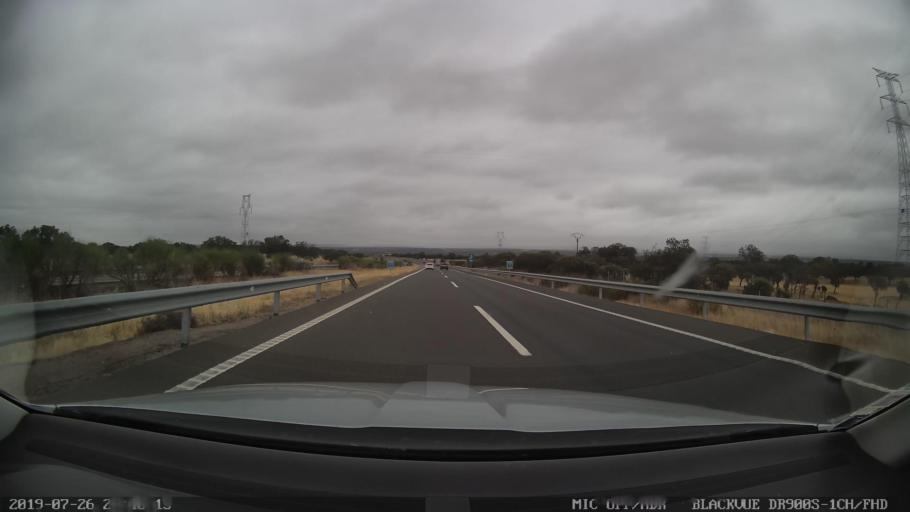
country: ES
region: Extremadura
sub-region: Provincia de Caceres
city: Jaraicejo
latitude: 39.5839
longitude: -5.8348
